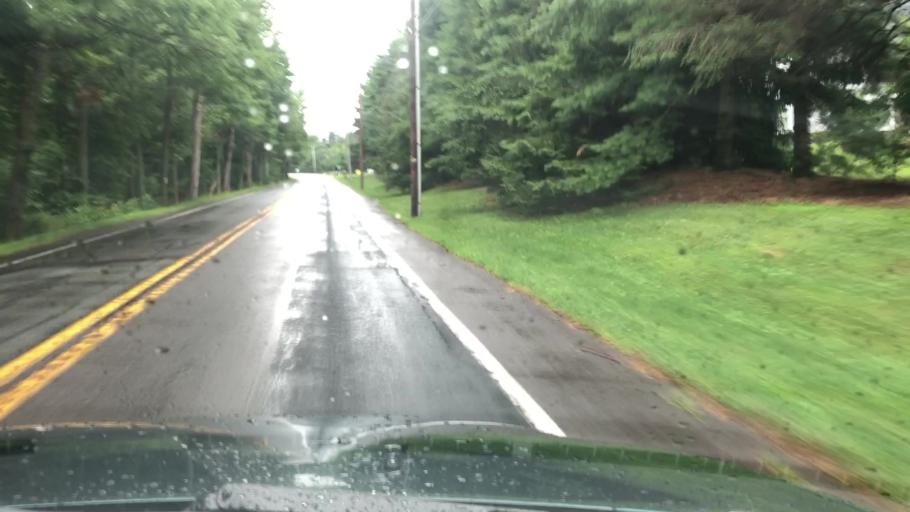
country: US
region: Pennsylvania
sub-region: Monroe County
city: Mountainhome
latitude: 41.2162
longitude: -75.2359
